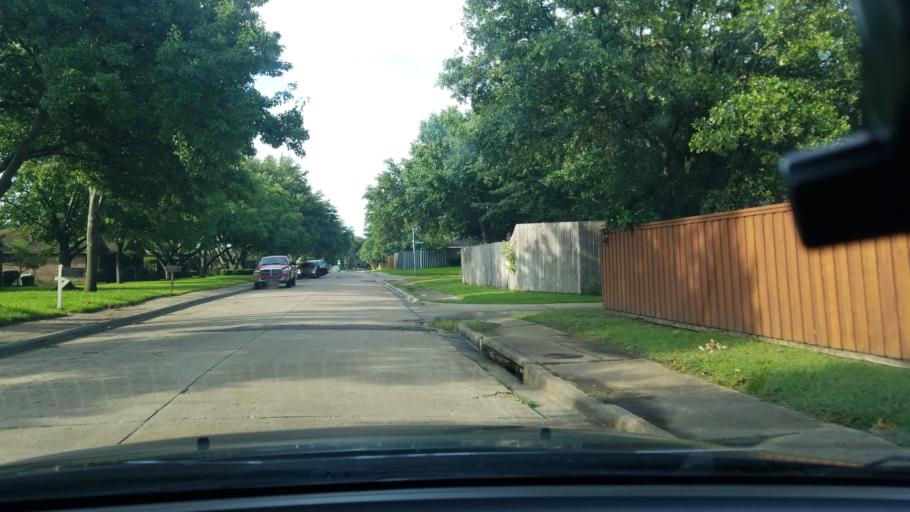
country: US
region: Texas
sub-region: Dallas County
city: Mesquite
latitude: 32.7997
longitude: -96.6065
